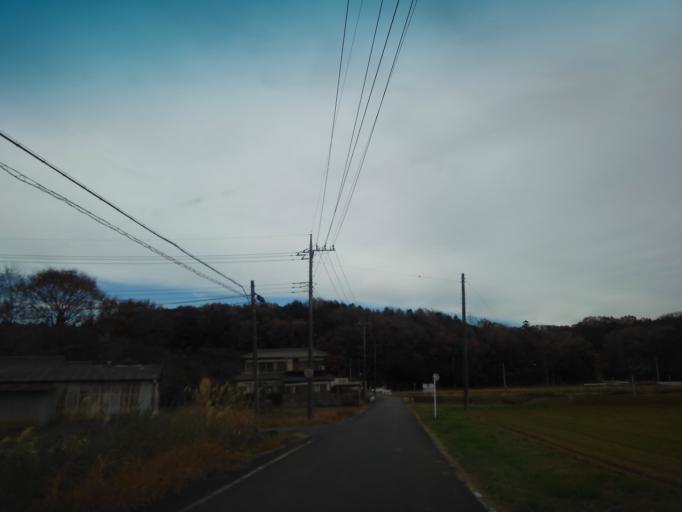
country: JP
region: Saitama
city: Morohongo
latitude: 35.9867
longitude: 139.3090
